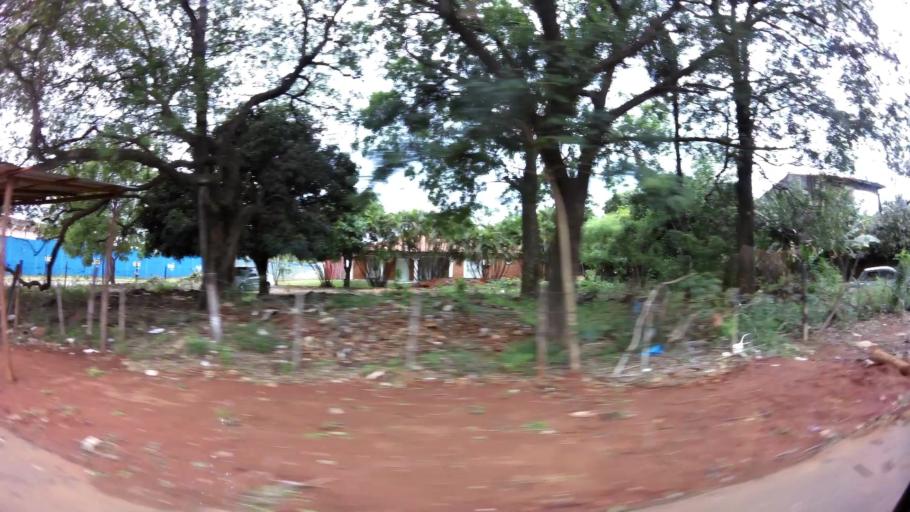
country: PY
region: Central
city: San Lorenzo
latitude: -25.2738
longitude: -57.4942
